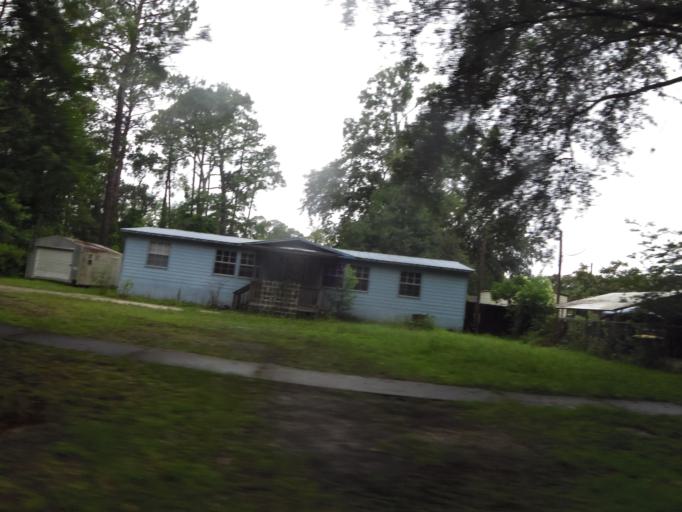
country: US
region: Florida
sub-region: Duval County
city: Jacksonville
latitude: 30.2778
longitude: -81.6198
